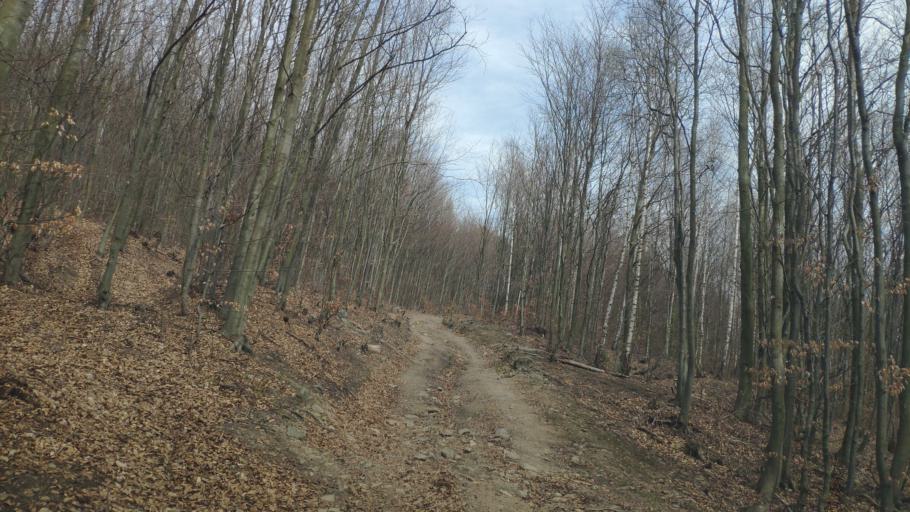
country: SK
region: Kosicky
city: Gelnica
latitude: 48.7519
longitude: 21.0191
